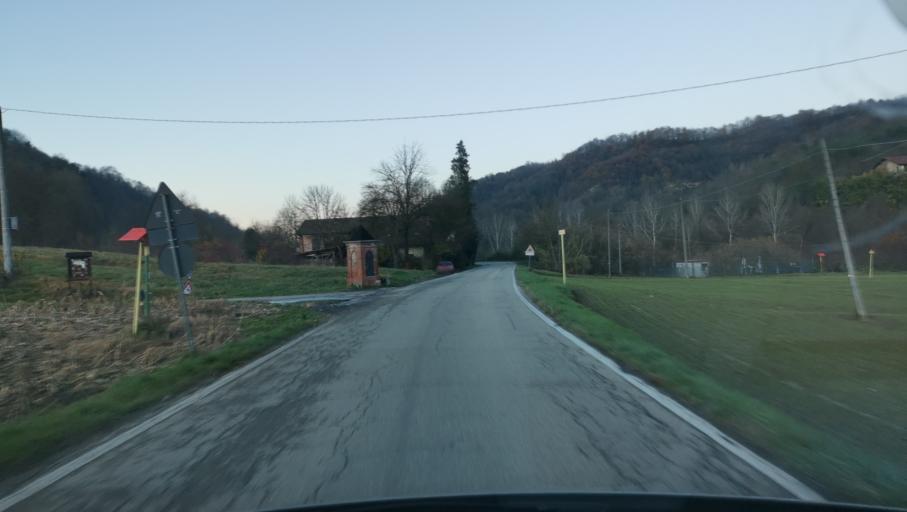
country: IT
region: Piedmont
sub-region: Provincia di Asti
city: Berzano di San Pietro
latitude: 45.1063
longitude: 7.9413
